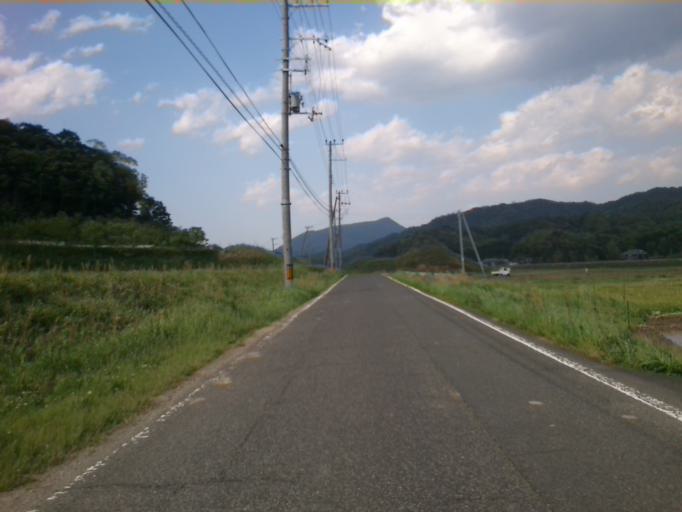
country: JP
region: Kyoto
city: Miyazu
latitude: 35.6833
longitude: 135.0923
